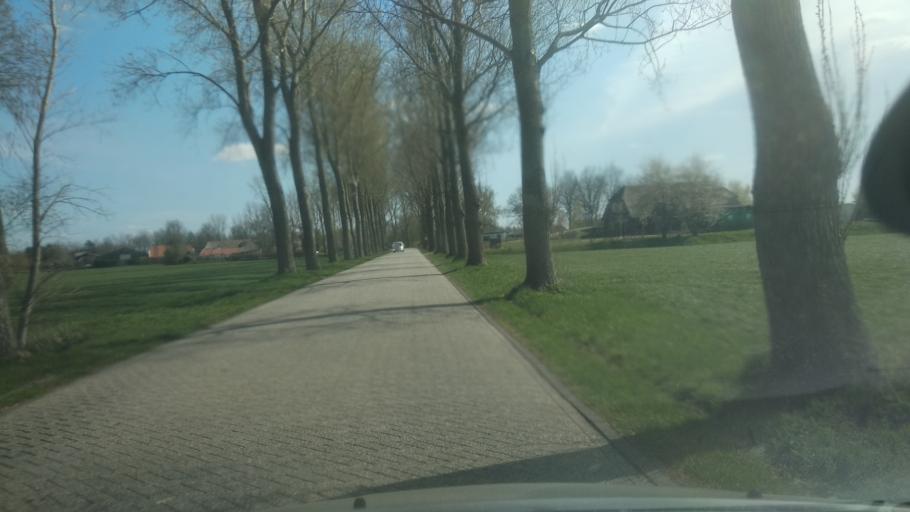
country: NL
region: Groningen
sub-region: Gemeente Stadskanaal
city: Stadskanaal
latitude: 52.9222
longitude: 6.8879
